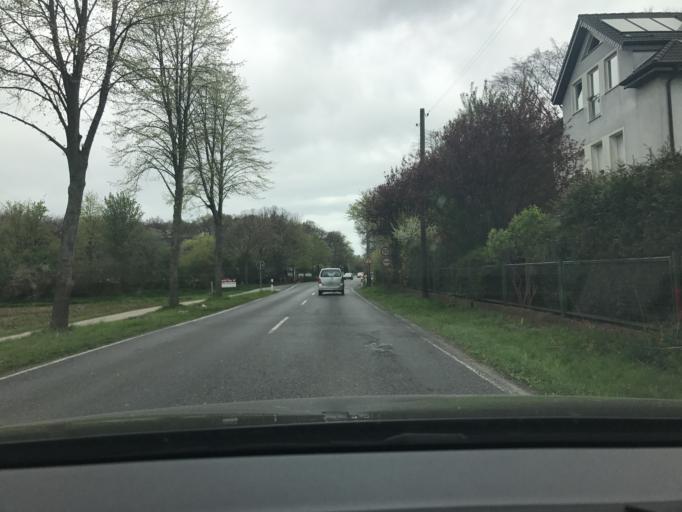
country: DE
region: North Rhine-Westphalia
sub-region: Regierungsbezirk Dusseldorf
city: Willich
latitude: 51.2973
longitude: 6.5321
